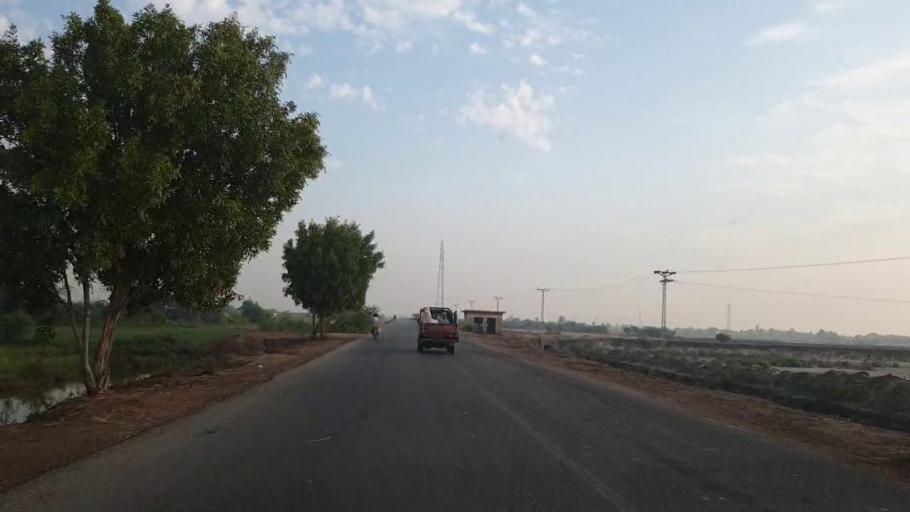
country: PK
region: Sindh
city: Badin
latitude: 24.6952
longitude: 68.9194
